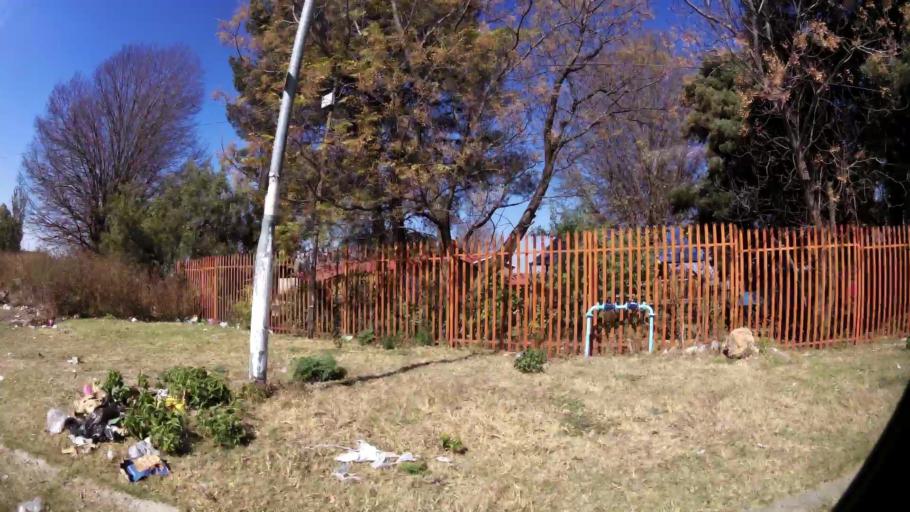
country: ZA
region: Gauteng
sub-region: City of Johannesburg Metropolitan Municipality
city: Soweto
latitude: -26.2419
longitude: 27.8968
